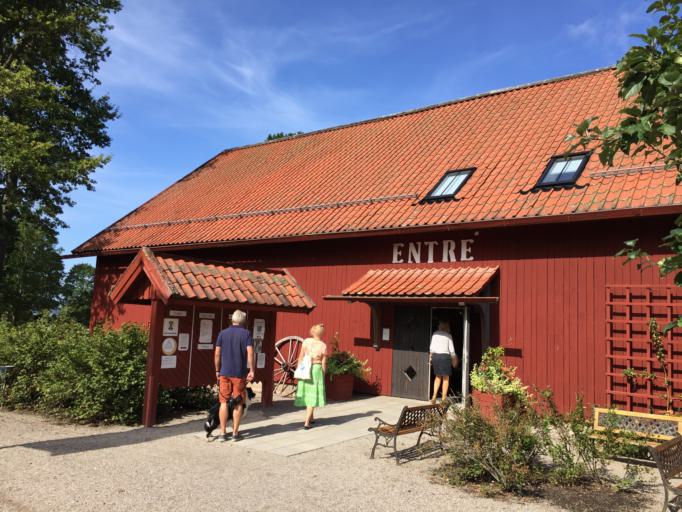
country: SE
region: Soedermanland
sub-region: Vingakers Kommun
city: Vingaker
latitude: 59.1483
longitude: 16.0451
